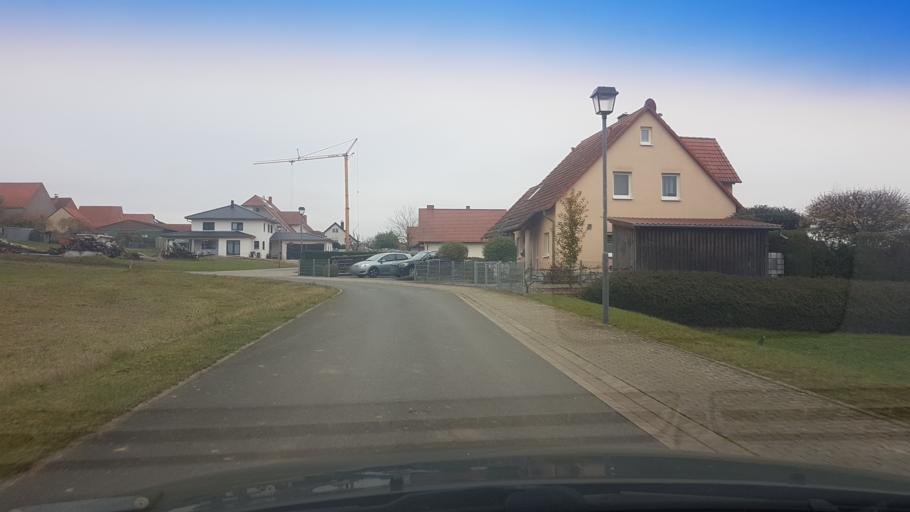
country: DE
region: Bavaria
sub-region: Upper Franconia
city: Rattelsdorf
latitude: 50.0194
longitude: 10.8754
